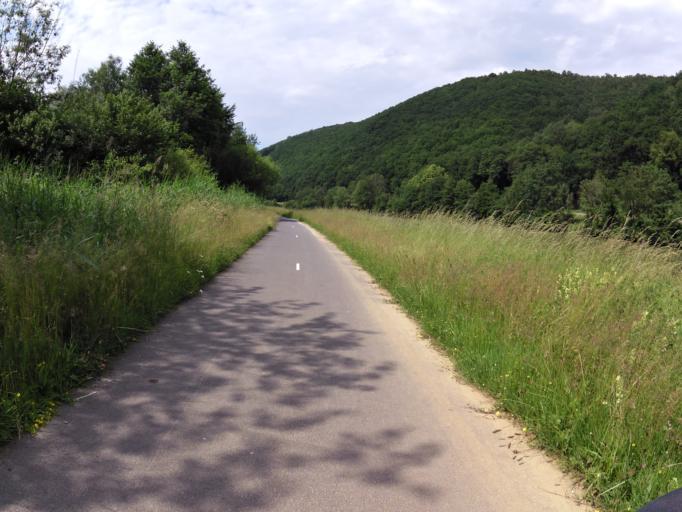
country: FR
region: Champagne-Ardenne
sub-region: Departement des Ardennes
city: Thilay
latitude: 49.8464
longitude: 4.7786
